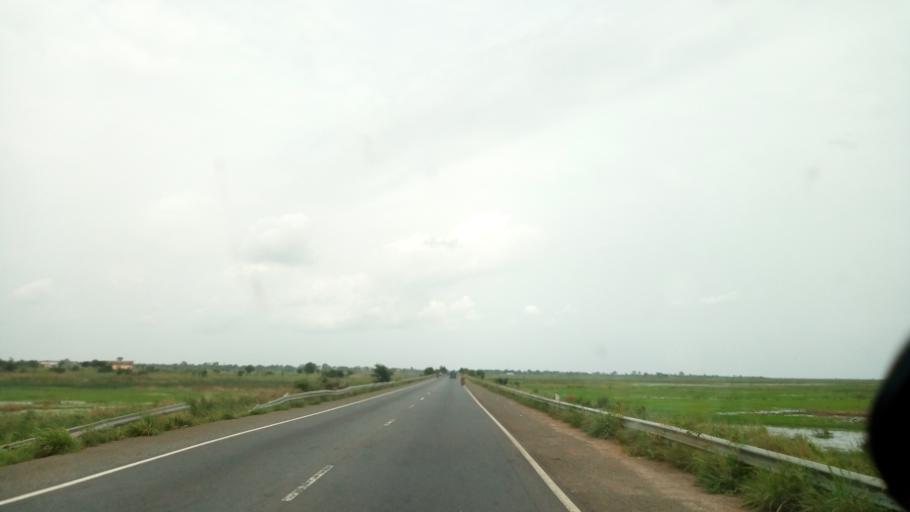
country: GH
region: Volta
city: Keta
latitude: 6.0634
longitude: 0.9234
